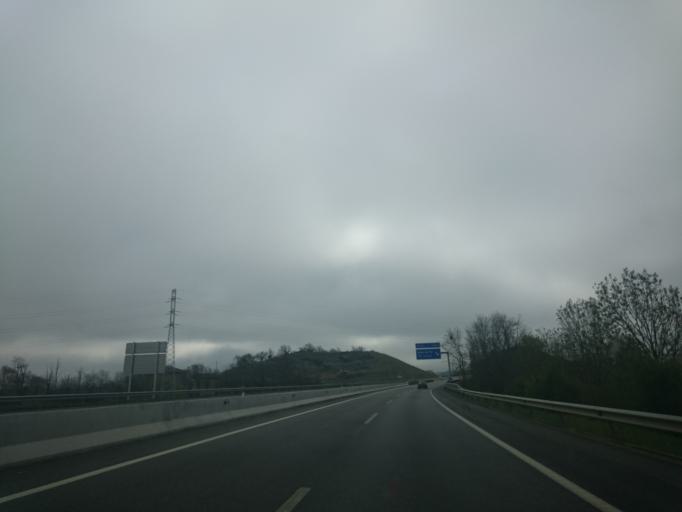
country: ES
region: Catalonia
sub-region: Provincia de Barcelona
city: Vic
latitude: 41.9602
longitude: 2.2772
